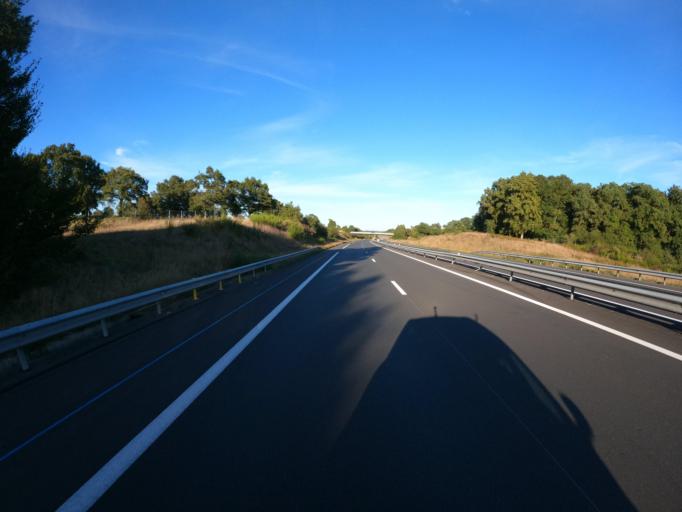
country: FR
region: Pays de la Loire
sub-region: Departement de la Vendee
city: Mortagne-sur-Sevre
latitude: 46.9569
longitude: -0.9368
